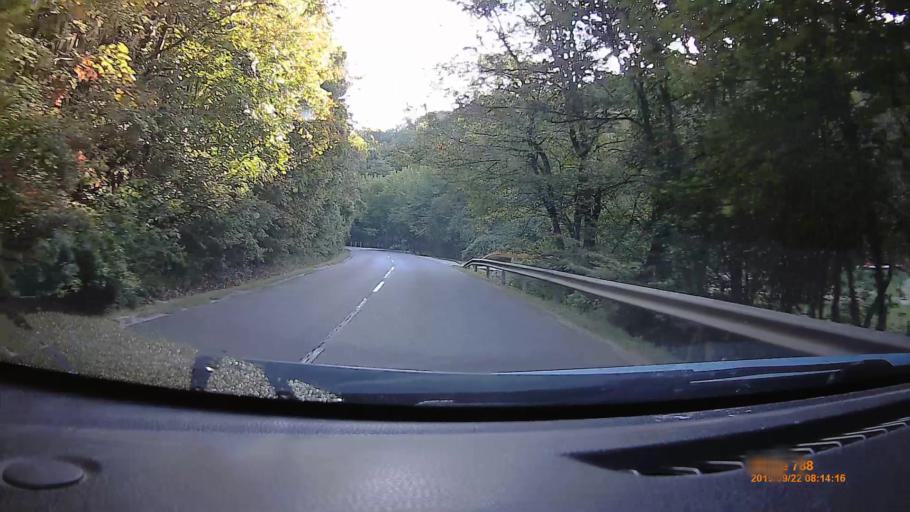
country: HU
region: Borsod-Abauj-Zemplen
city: Sajobabony
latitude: 48.1112
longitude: 20.6478
